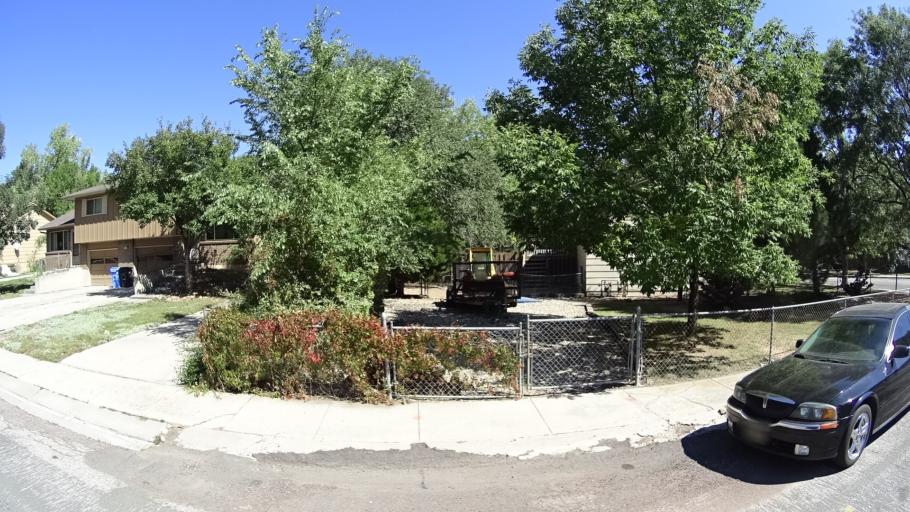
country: US
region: Colorado
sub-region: El Paso County
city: Colorado Springs
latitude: 38.8608
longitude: -104.8596
